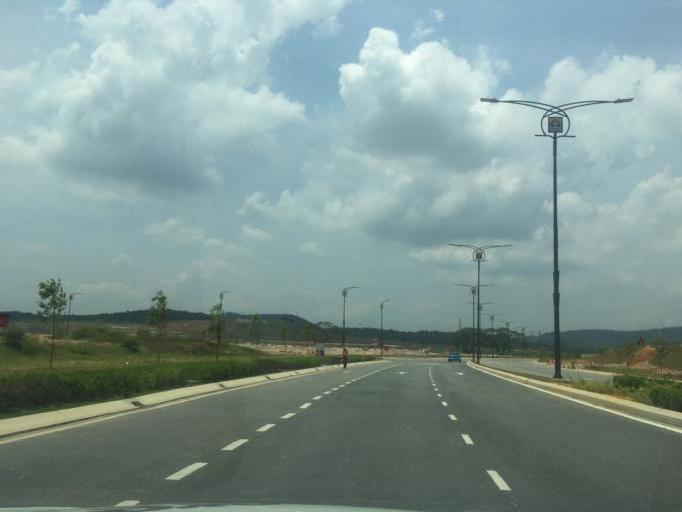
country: MY
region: Putrajaya
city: Putrajaya
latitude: 2.8453
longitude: 101.7015
